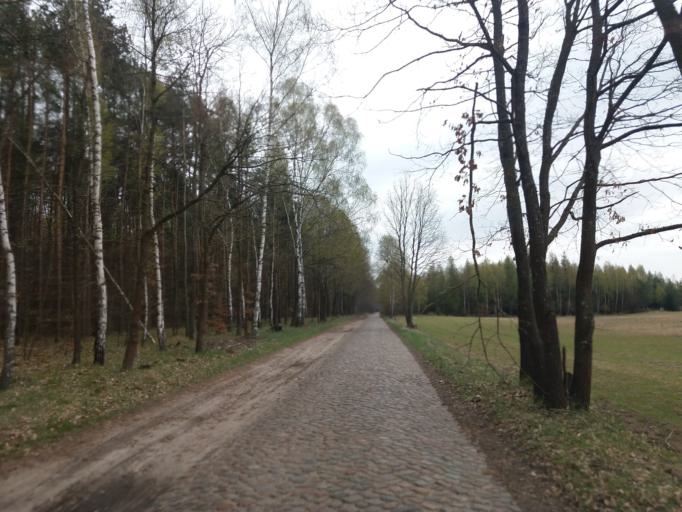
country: PL
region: Lubusz
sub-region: Powiat strzelecko-drezdenecki
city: Dobiegniew
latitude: 53.0902
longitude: 15.7971
